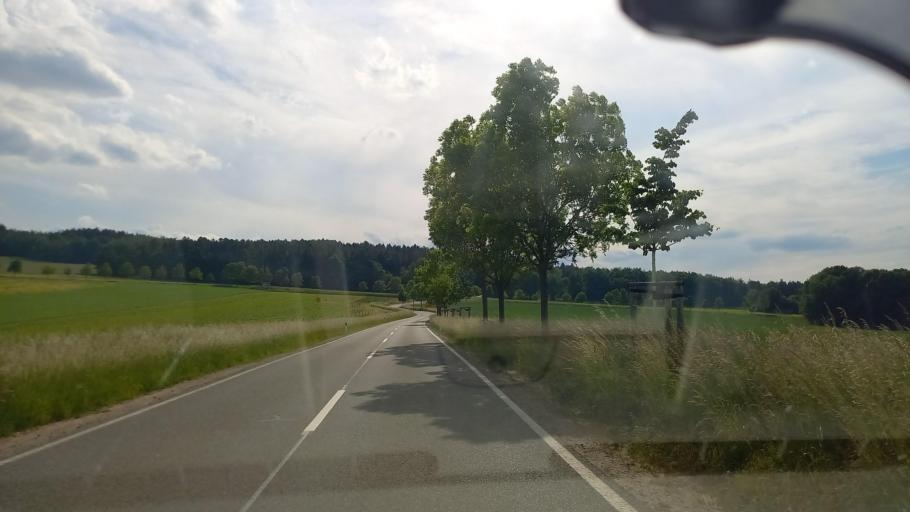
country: DE
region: Saxony
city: Wildenfels
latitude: 50.6282
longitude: 12.5774
